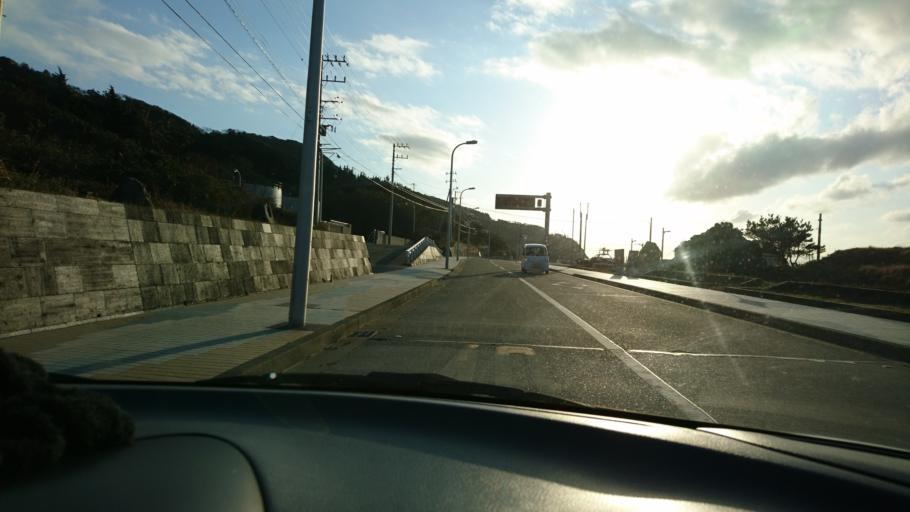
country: JP
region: Shizuoka
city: Shimoda
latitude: 34.3707
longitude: 139.2495
